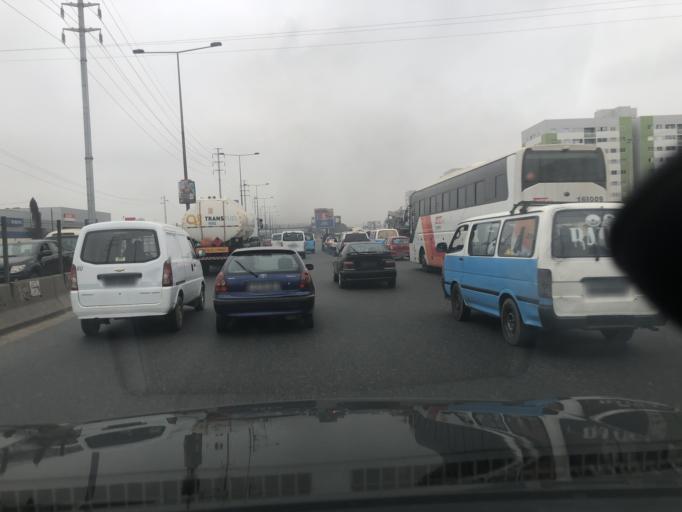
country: AO
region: Luanda
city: Luanda
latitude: -8.8506
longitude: 13.2878
